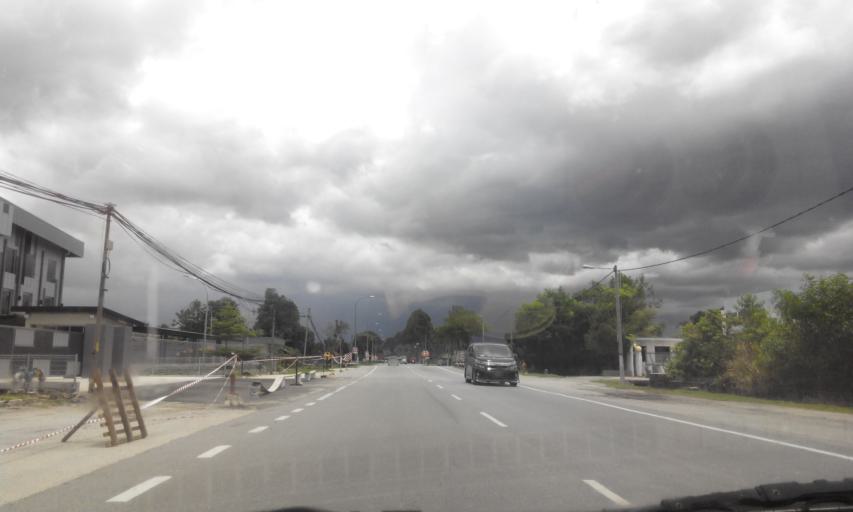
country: MY
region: Perak
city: Parit Buntar
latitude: 5.1084
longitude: 100.4892
